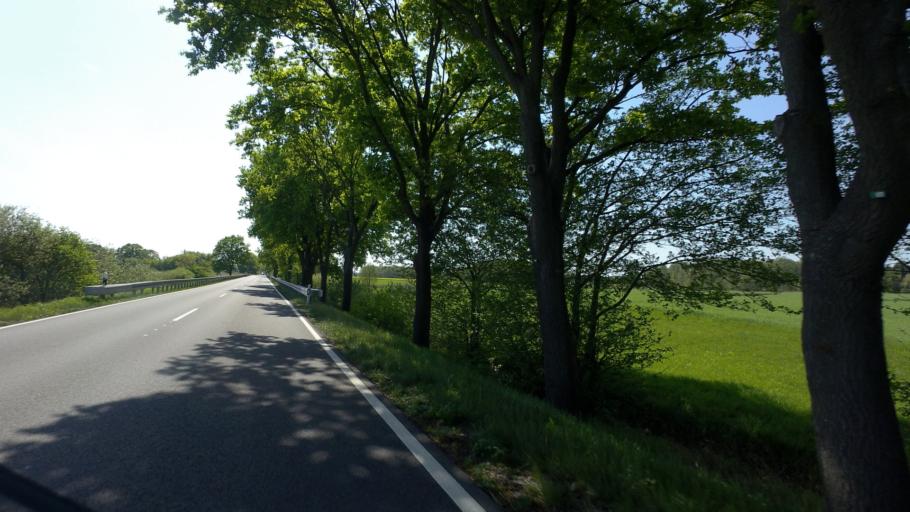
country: DE
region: Brandenburg
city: Neu Zauche
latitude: 52.0248
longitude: 14.0836
